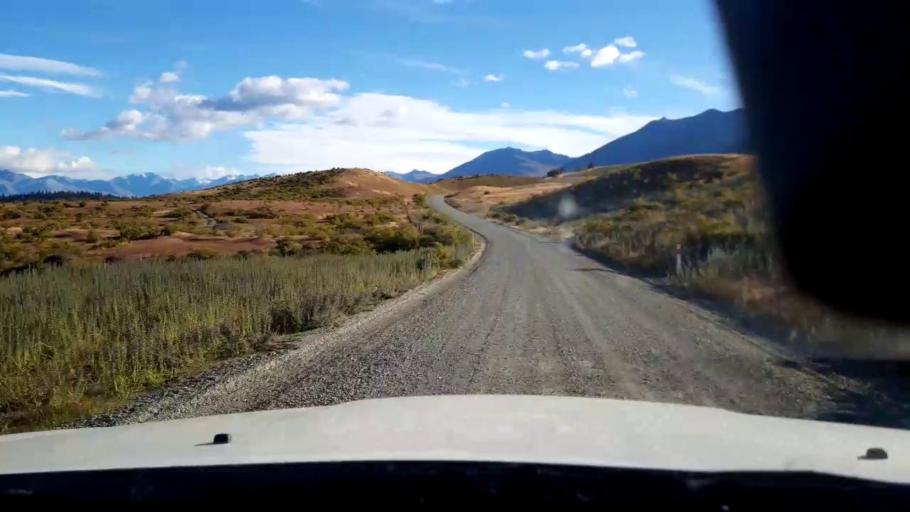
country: NZ
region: Canterbury
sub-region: Timaru District
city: Pleasant Point
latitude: -43.9694
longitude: 170.5150
